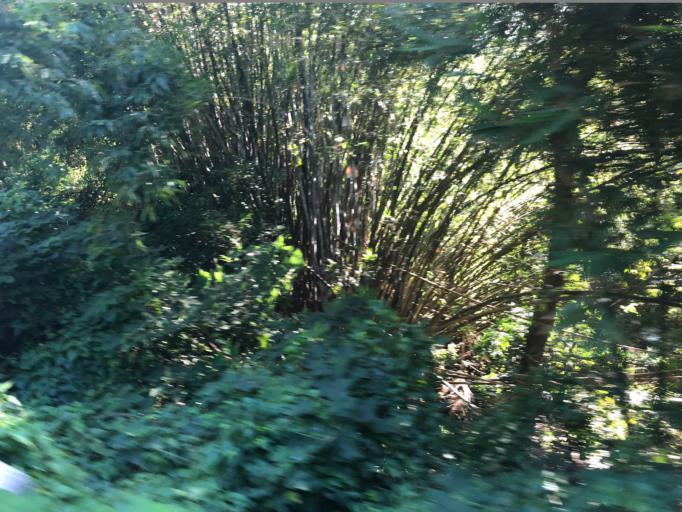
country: TW
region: Taiwan
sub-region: Hsinchu
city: Hsinchu
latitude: 24.7510
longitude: 120.9769
